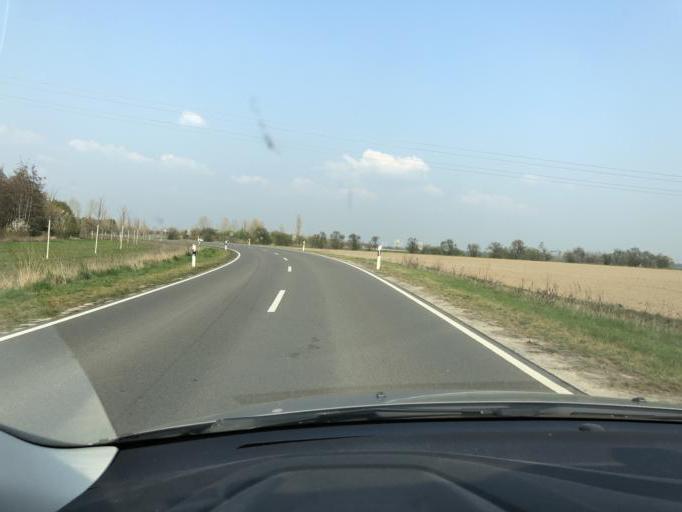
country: DE
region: Saxony
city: Zwochau
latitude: 51.4214
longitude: 12.3142
